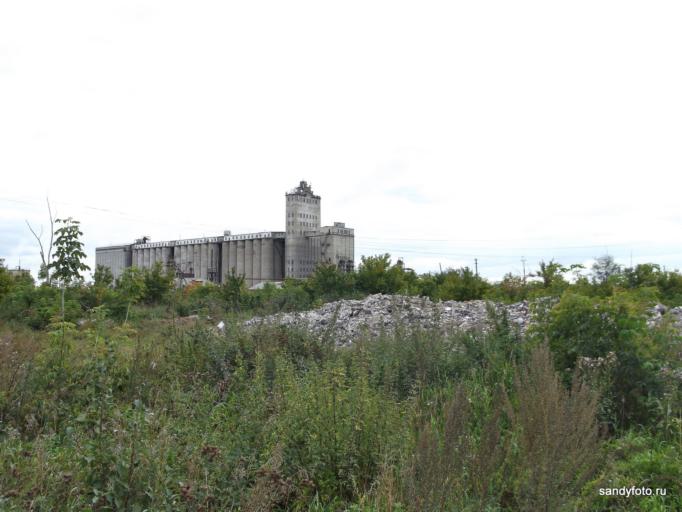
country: RU
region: Chelyabinsk
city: Troitsk
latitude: 54.1095
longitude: 61.5941
